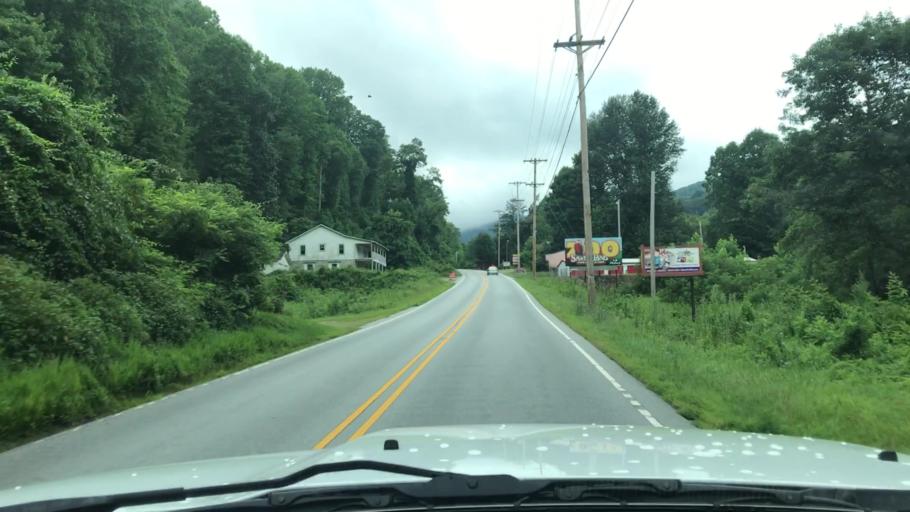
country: US
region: North Carolina
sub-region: Haywood County
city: Maggie Valley
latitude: 35.5226
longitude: -83.1172
